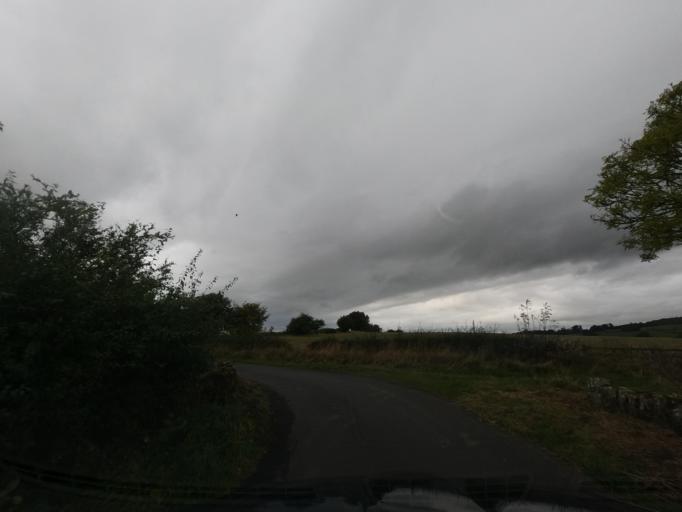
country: GB
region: England
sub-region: Northumberland
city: Ford
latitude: 55.6200
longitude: -2.0787
